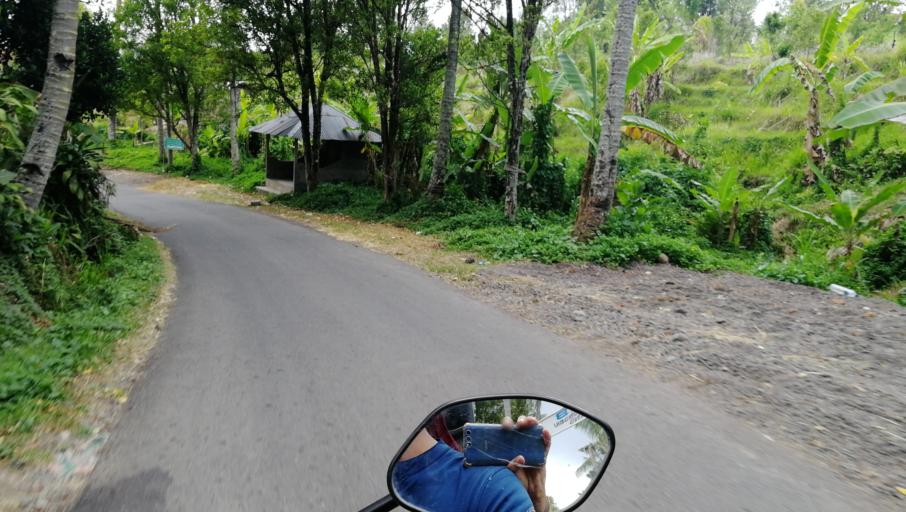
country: ID
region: Bali
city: Puspajati
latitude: -8.2720
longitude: 115.0148
